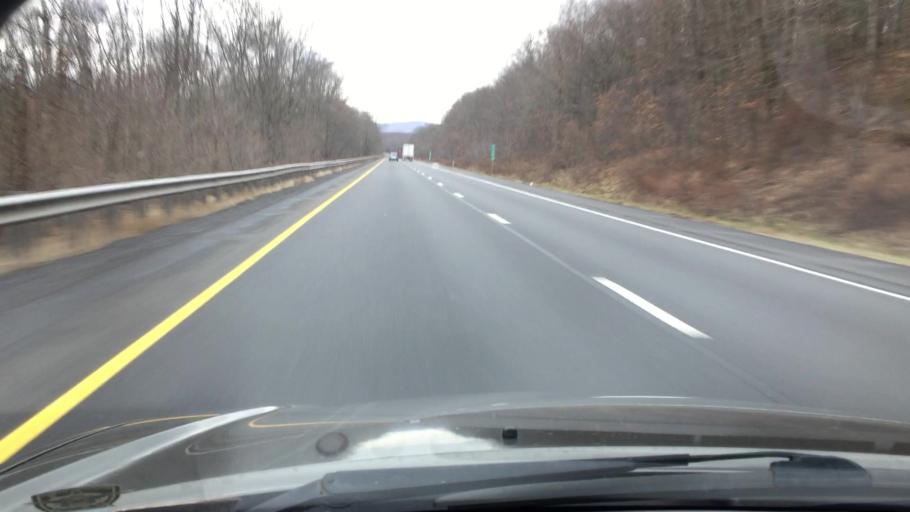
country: US
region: Pennsylvania
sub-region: Luzerne County
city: Freeland
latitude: 41.0616
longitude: -75.8841
